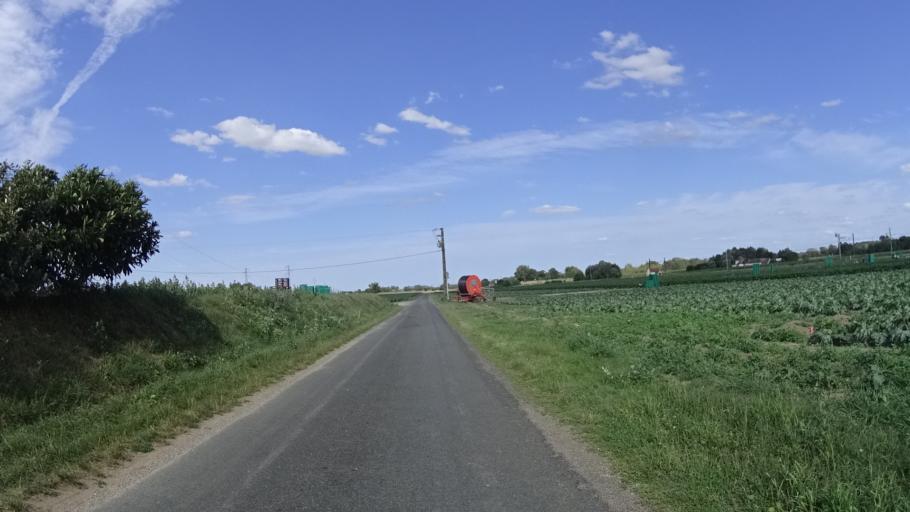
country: FR
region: Centre
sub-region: Departement d'Indre-et-Loire
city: Cangey
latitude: 47.4625
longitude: 1.0752
